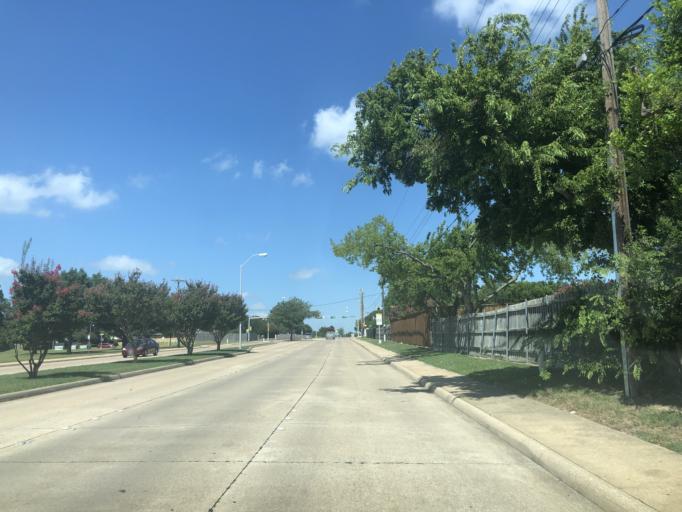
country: US
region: Texas
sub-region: Dallas County
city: Duncanville
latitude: 32.6475
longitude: -96.9320
